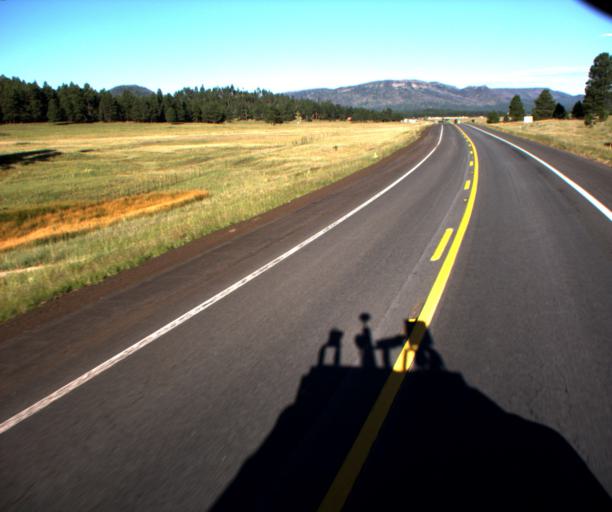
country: US
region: New Mexico
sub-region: Catron County
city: Reserve
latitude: 33.8265
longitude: -109.0837
